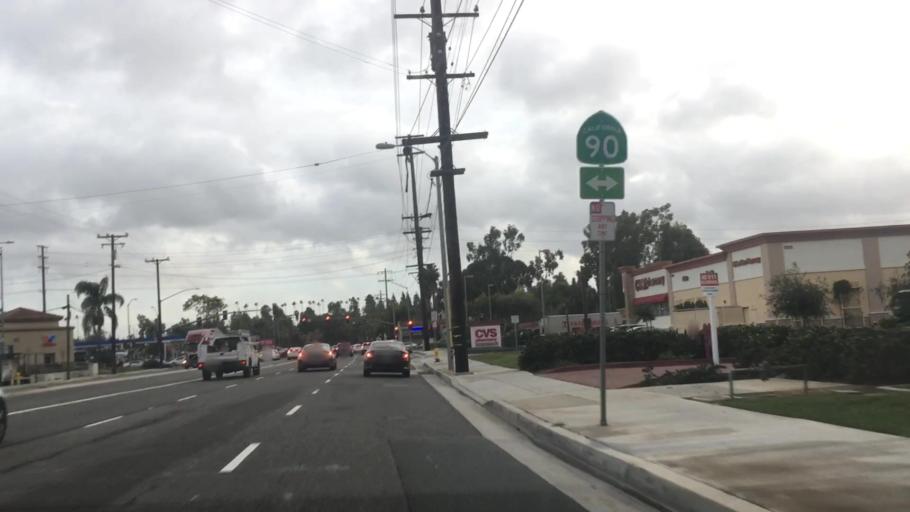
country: US
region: California
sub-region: Orange County
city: La Habra
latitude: 33.9183
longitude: -117.9332
